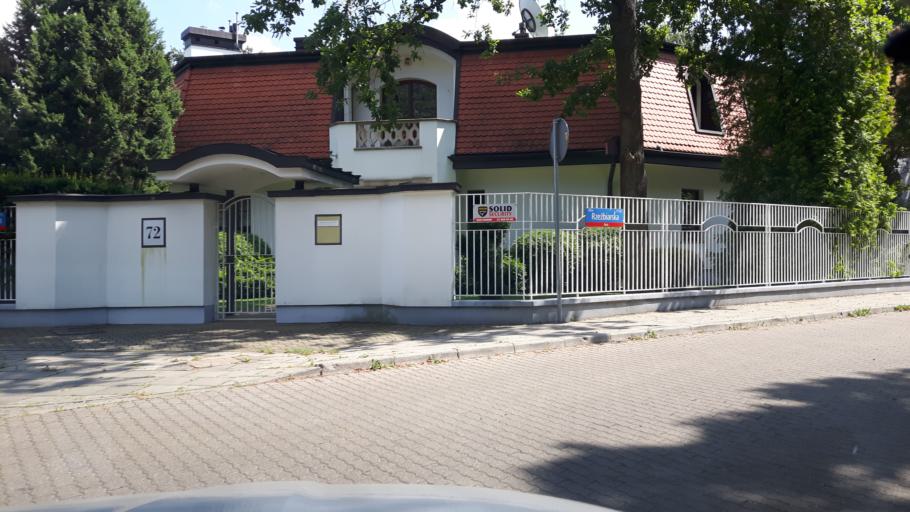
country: PL
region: Masovian Voivodeship
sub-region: Warszawa
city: Wawer
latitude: 52.2226
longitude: 21.1604
